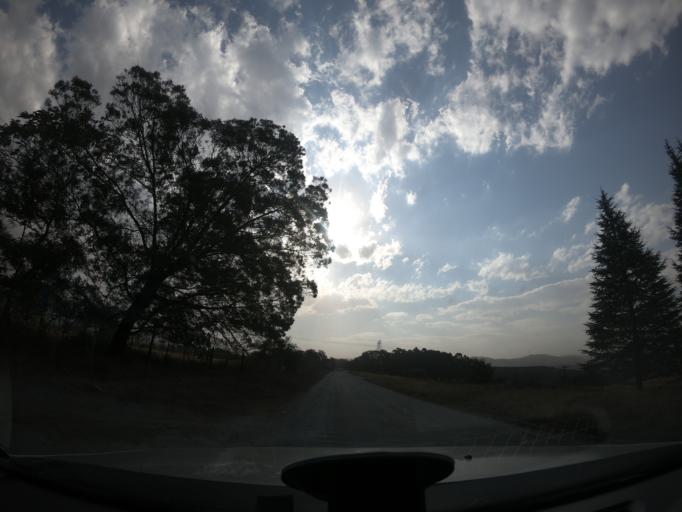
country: ZA
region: KwaZulu-Natal
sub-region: uMgungundlovu District Municipality
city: Howick
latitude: -29.4341
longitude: 30.1124
